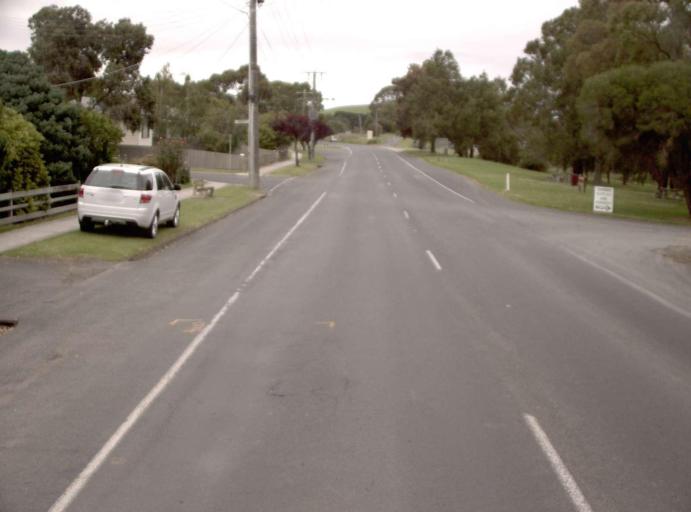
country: AU
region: Victoria
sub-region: Bass Coast
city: North Wonthaggi
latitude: -38.4389
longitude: 145.8281
